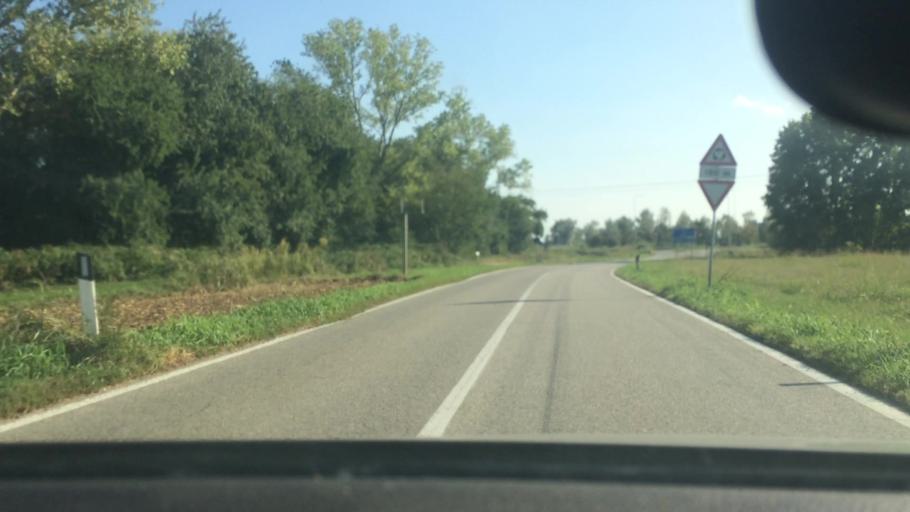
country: IT
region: Lombardy
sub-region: Citta metropolitana di Milano
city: Buscate
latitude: 45.5297
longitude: 8.8098
